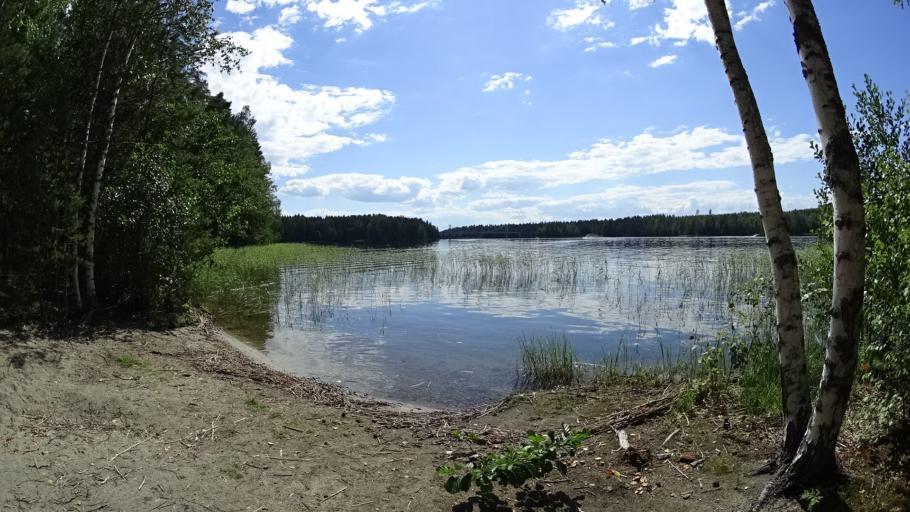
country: FI
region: Southern Savonia
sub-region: Savonlinna
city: Punkaharju
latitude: 61.7923
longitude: 29.3034
